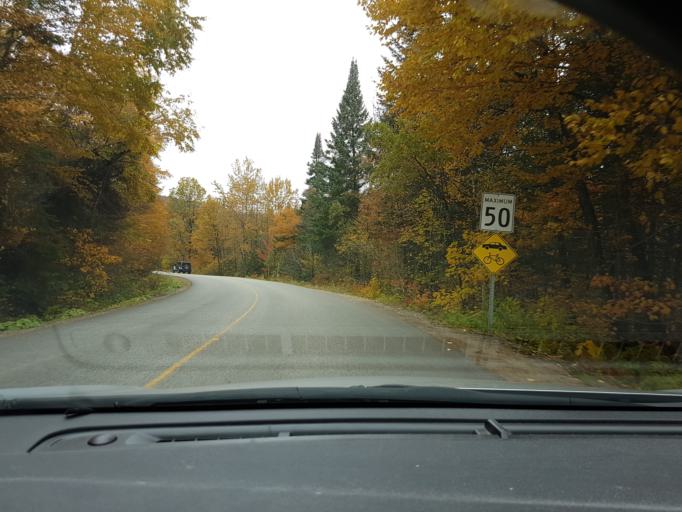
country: CA
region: Quebec
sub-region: Capitale-Nationale
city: Shannon
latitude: 47.1106
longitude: -71.3478
